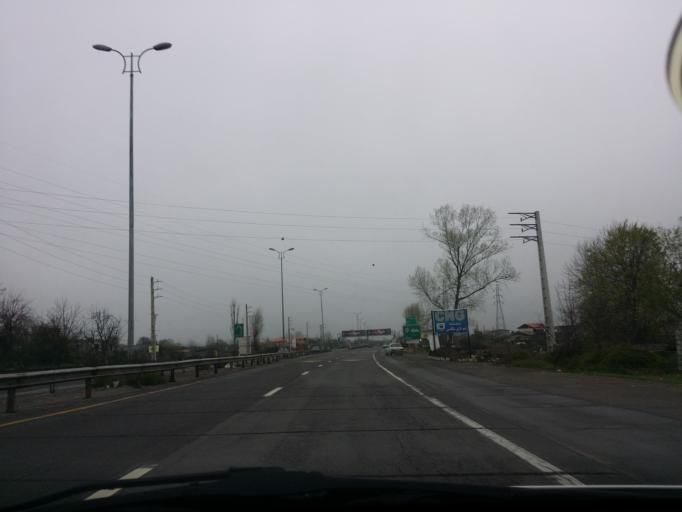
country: IR
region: Mazandaran
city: Tonekabon
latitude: 36.8124
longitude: 50.8560
